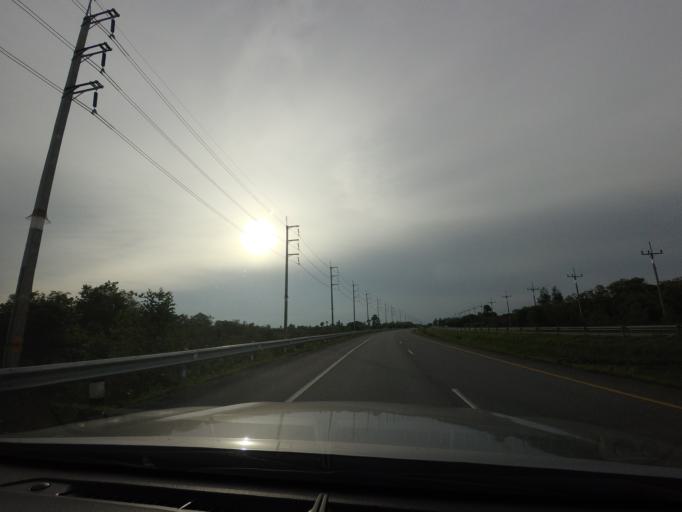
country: TH
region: Nakhon Si Thammarat
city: Hua Sai
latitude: 7.9990
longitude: 100.3066
